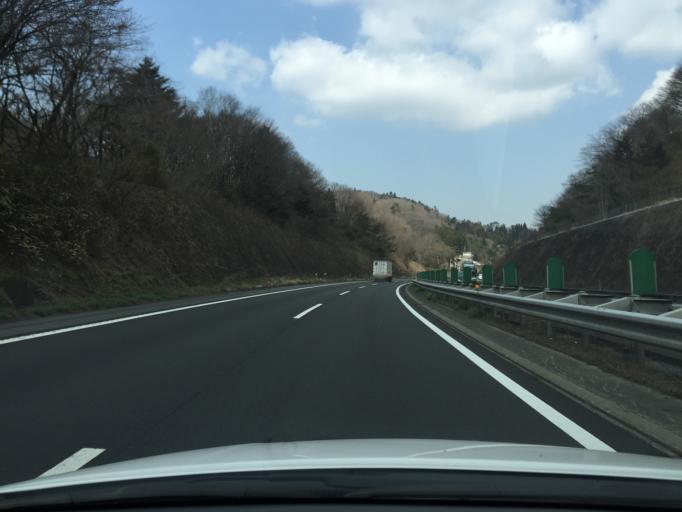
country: JP
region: Miyagi
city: Sendai
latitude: 38.2522
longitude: 140.8140
